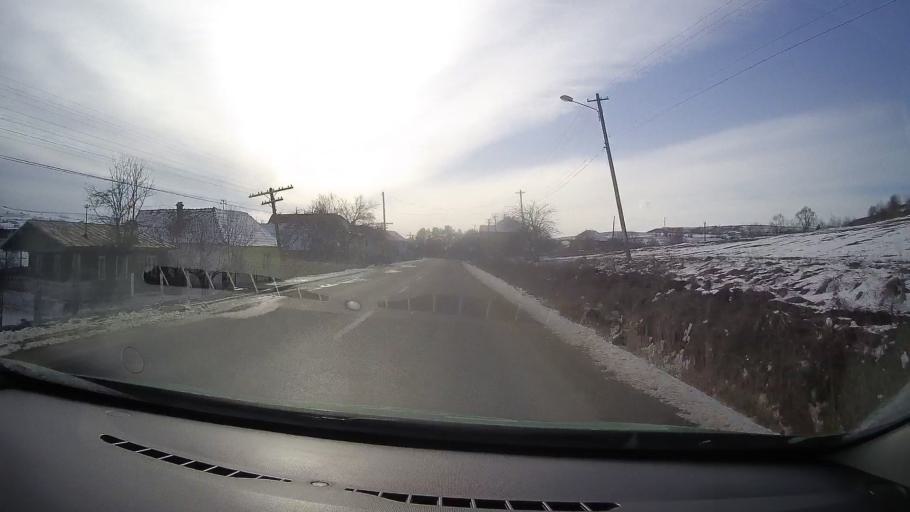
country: RO
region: Sibiu
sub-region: Oras Agnita
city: Ruja
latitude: 45.9855
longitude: 24.6482
